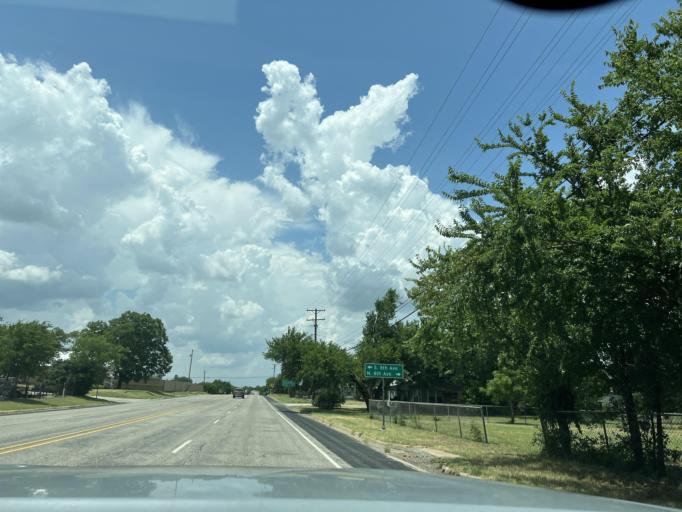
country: US
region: Texas
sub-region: Palo Pinto County
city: Palo Pinto
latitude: 32.7681
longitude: -98.3020
